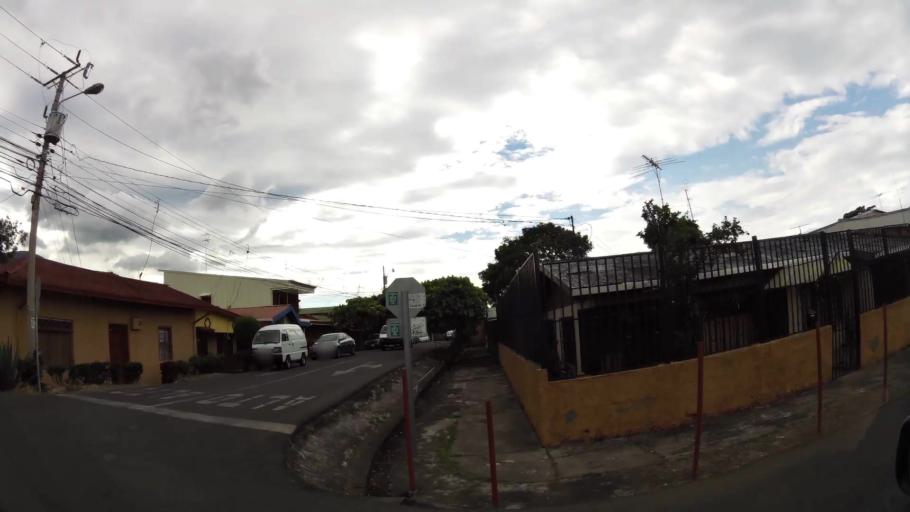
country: CR
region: San Jose
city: Santa Ana
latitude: 9.9333
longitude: -84.1837
